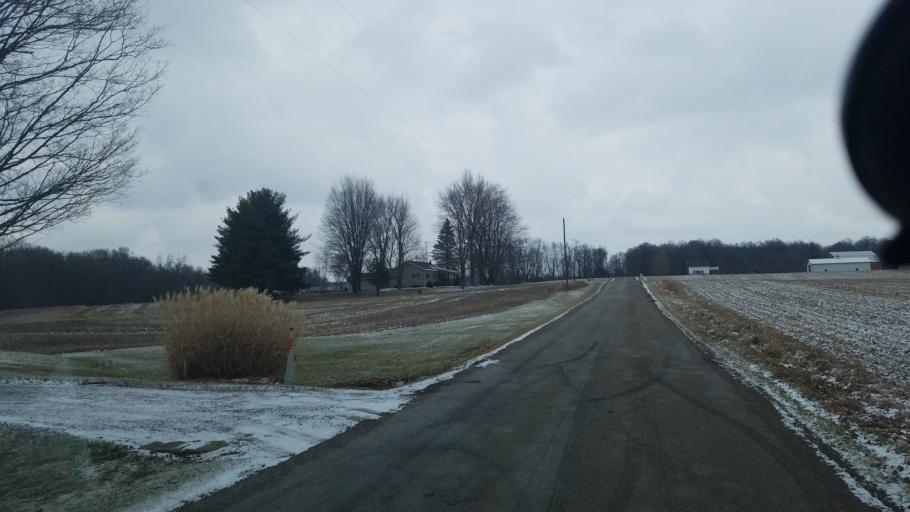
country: US
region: Ohio
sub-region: Morrow County
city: Mount Gilead
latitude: 40.5855
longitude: -82.7846
